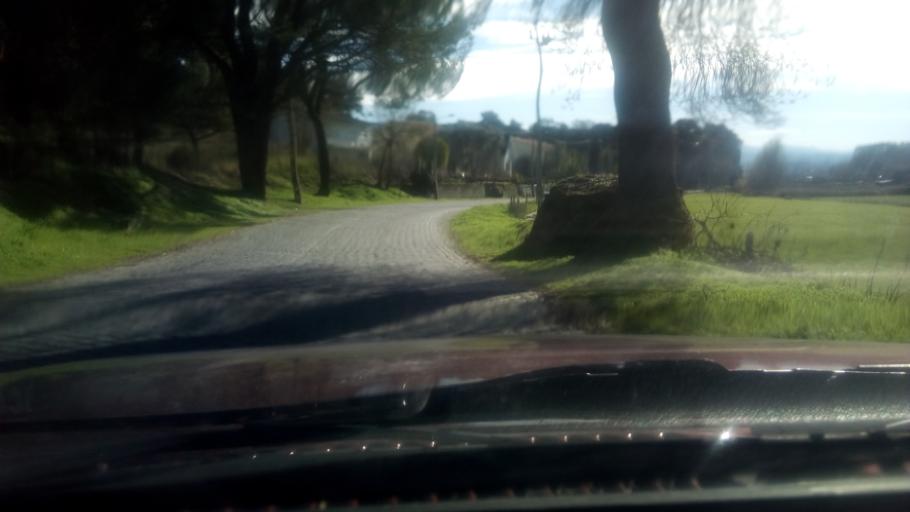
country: PT
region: Guarda
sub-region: Fornos de Algodres
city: Fornos de Algodres
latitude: 40.6206
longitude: -7.5301
